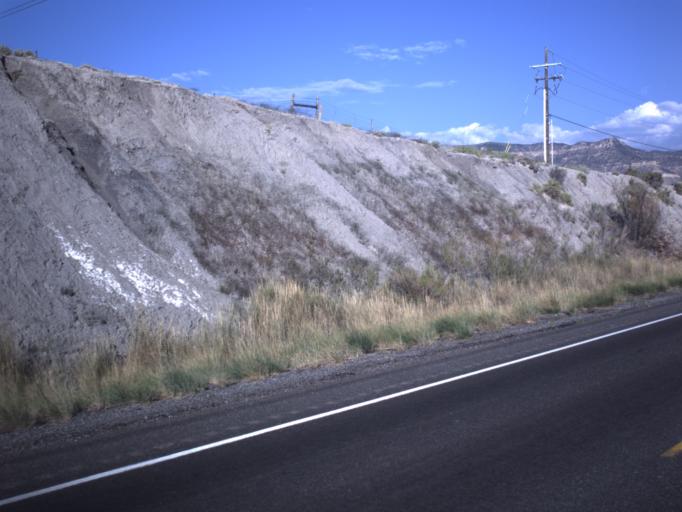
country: US
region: Utah
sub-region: Emery County
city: Huntington
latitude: 39.3457
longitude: -110.9899
